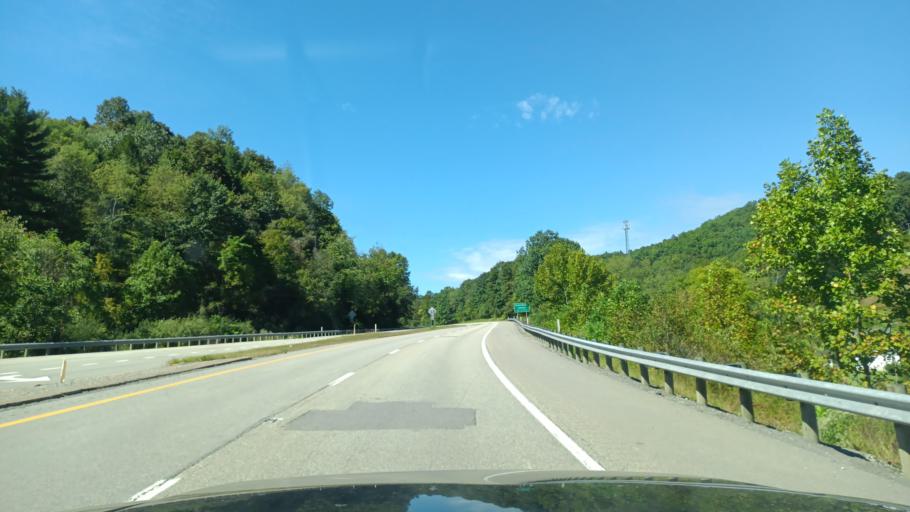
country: US
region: West Virginia
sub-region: Harrison County
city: Salem
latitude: 39.2898
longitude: -80.4981
